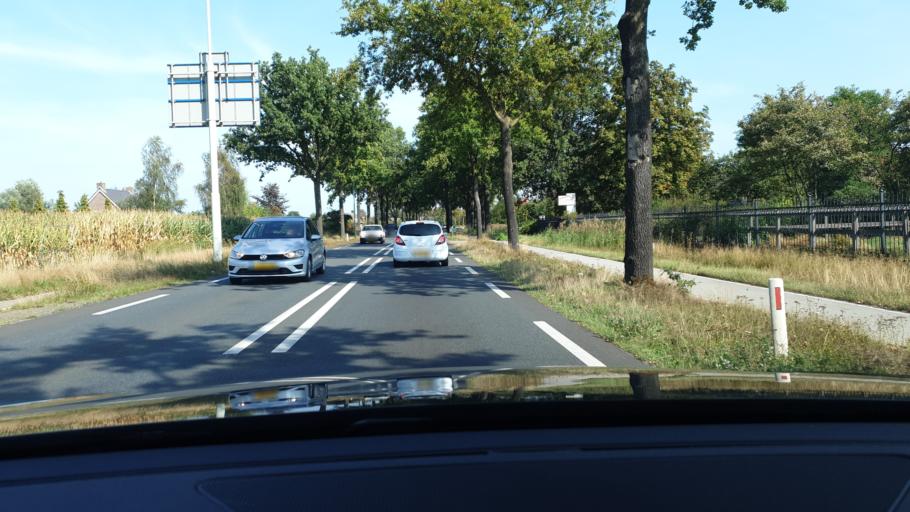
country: NL
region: North Brabant
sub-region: Gemeente Laarbeek
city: Aarle-Rixtel
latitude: 51.5193
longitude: 5.6083
